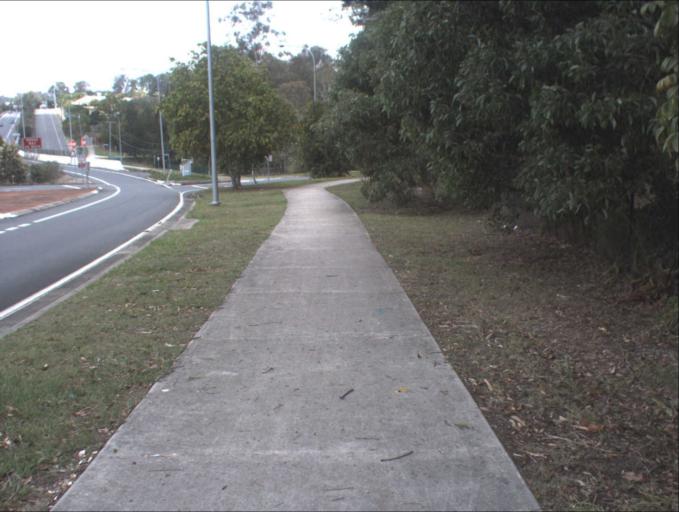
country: AU
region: Queensland
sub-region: Logan
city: Park Ridge South
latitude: -27.6876
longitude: 153.0317
